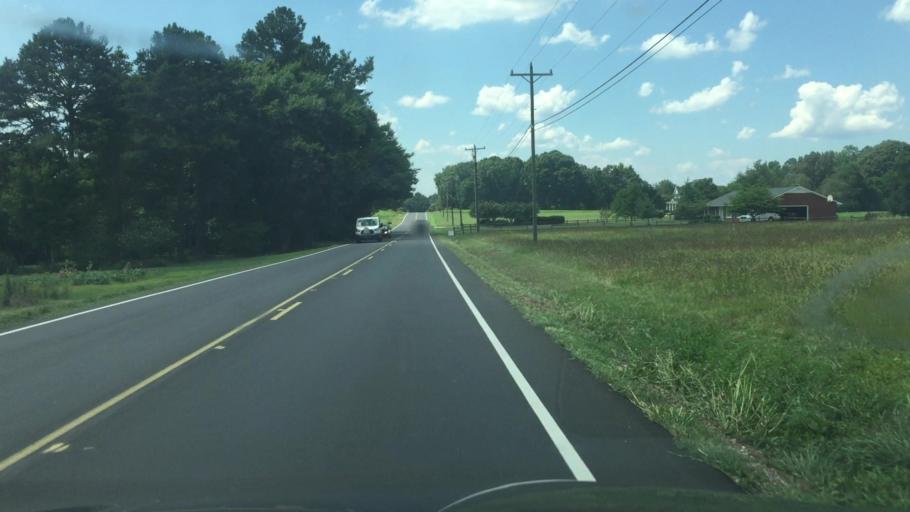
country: US
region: North Carolina
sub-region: Iredell County
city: Mooresville
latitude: 35.5932
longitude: -80.7582
